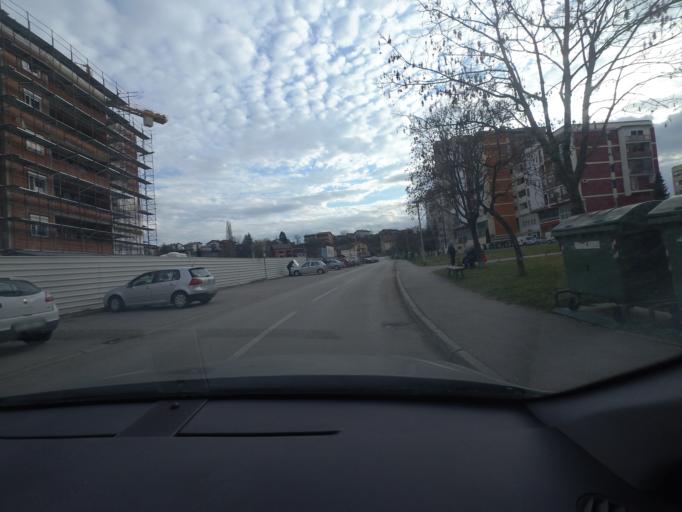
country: HR
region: Karlovacka
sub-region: Grad Karlovac
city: Karlovac
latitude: 45.4813
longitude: 15.5503
